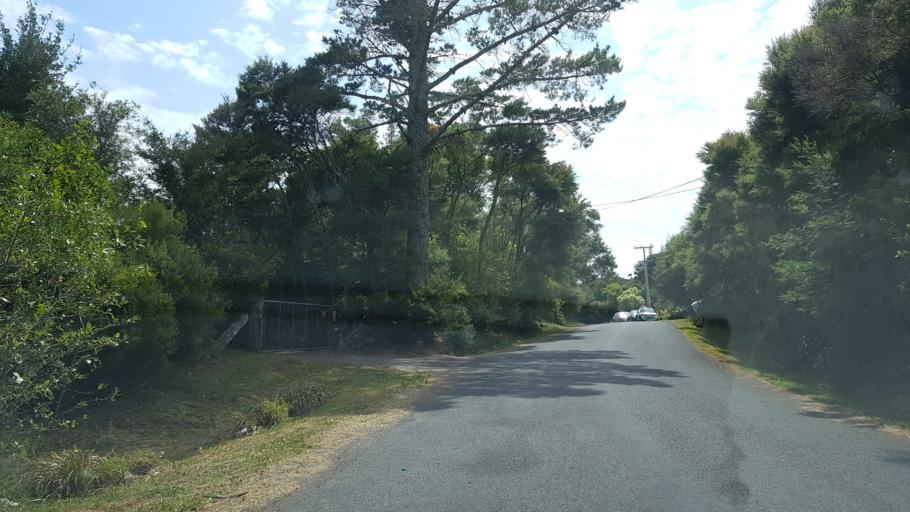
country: NZ
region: Auckland
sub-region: Auckland
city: North Shore
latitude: -36.7833
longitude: 174.6769
